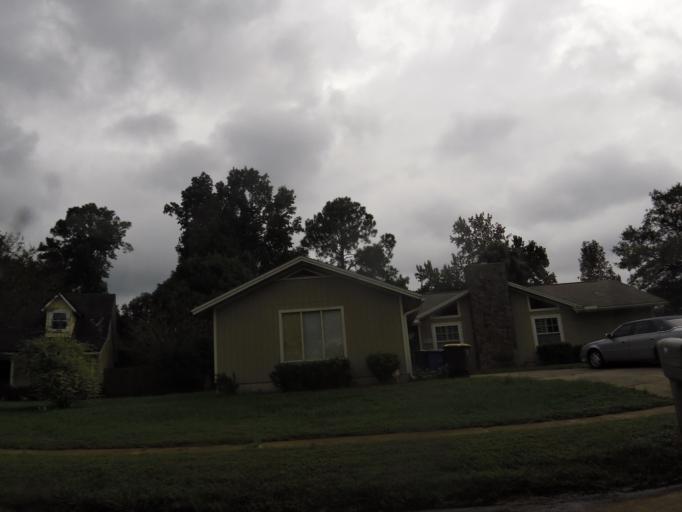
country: US
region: Florida
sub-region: Clay County
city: Bellair-Meadowbrook Terrace
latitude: 30.1929
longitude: -81.7656
